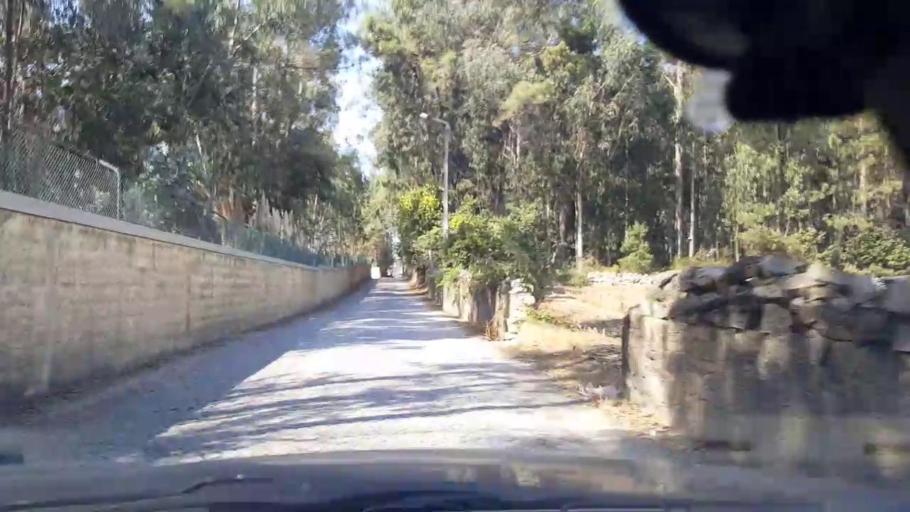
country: PT
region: Porto
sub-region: Povoa de Varzim
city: Pedroso
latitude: 41.3922
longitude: -8.7129
